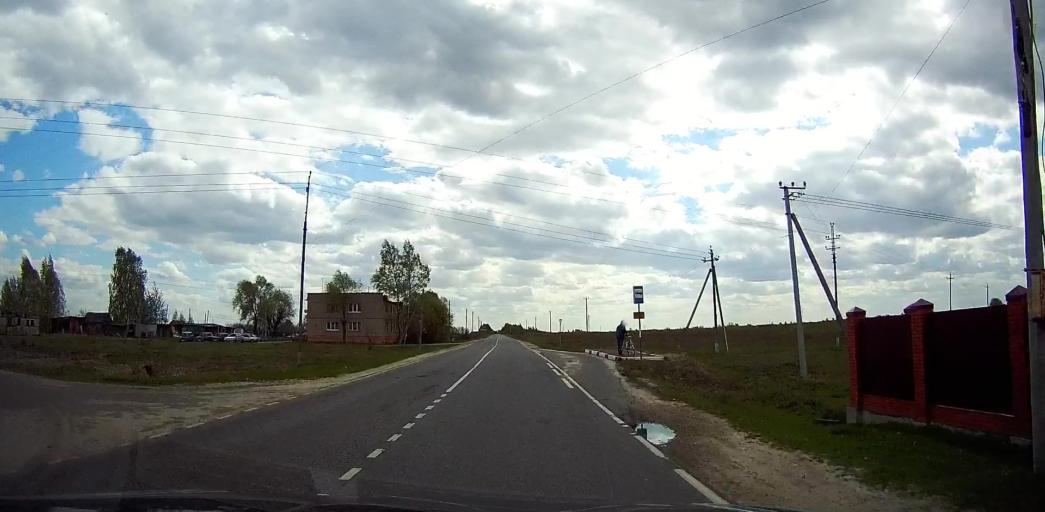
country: RU
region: Moskovskaya
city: Davydovo
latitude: 55.6434
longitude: 38.7502
